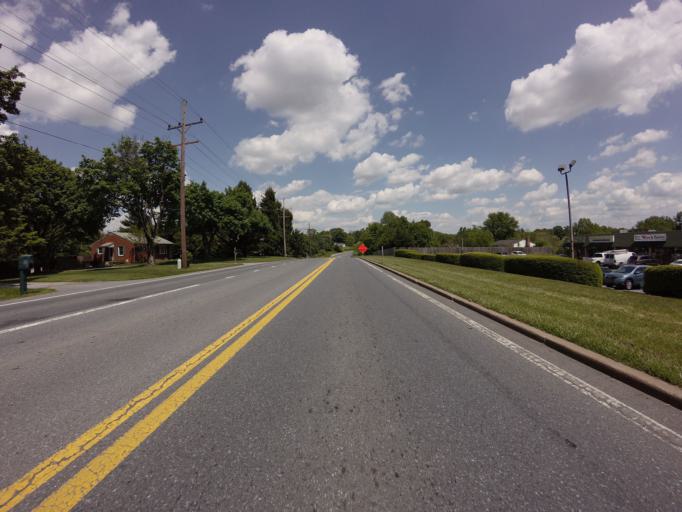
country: US
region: Maryland
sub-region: Frederick County
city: Green Valley
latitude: 39.3435
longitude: -77.2578
